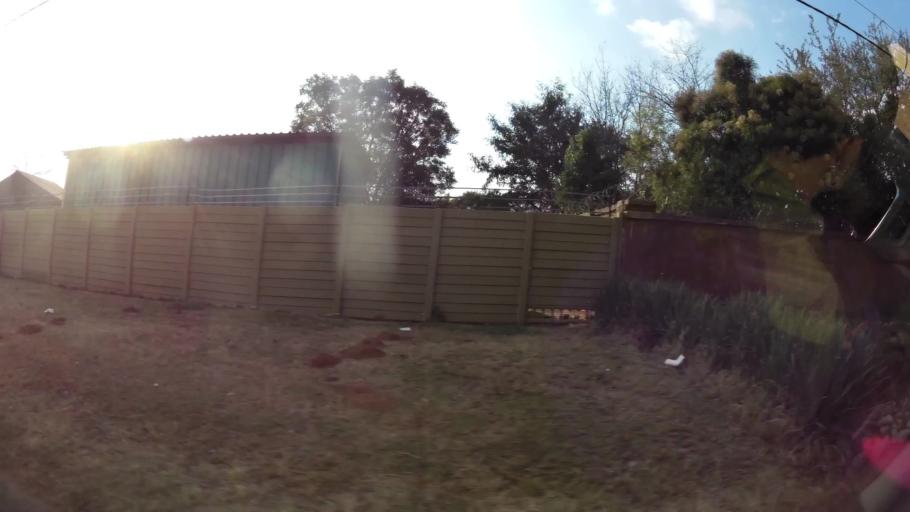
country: ZA
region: Gauteng
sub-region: Ekurhuleni Metropolitan Municipality
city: Benoni
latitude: -26.1200
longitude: 28.2994
